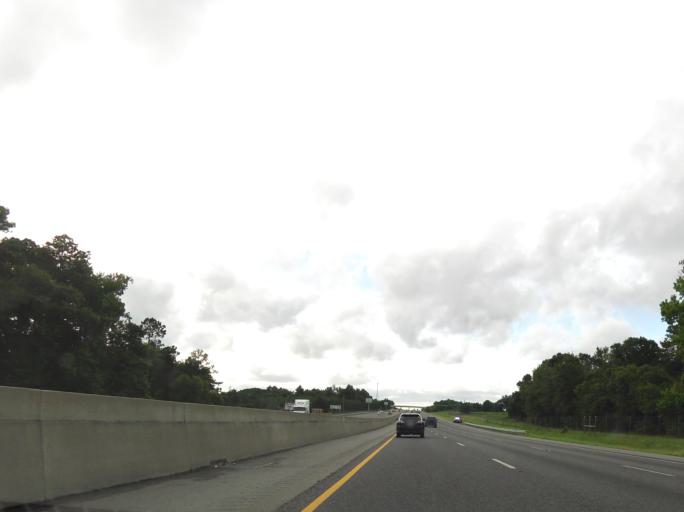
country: US
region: Georgia
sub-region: Turner County
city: Ashburn
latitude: 31.6387
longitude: -83.5860
